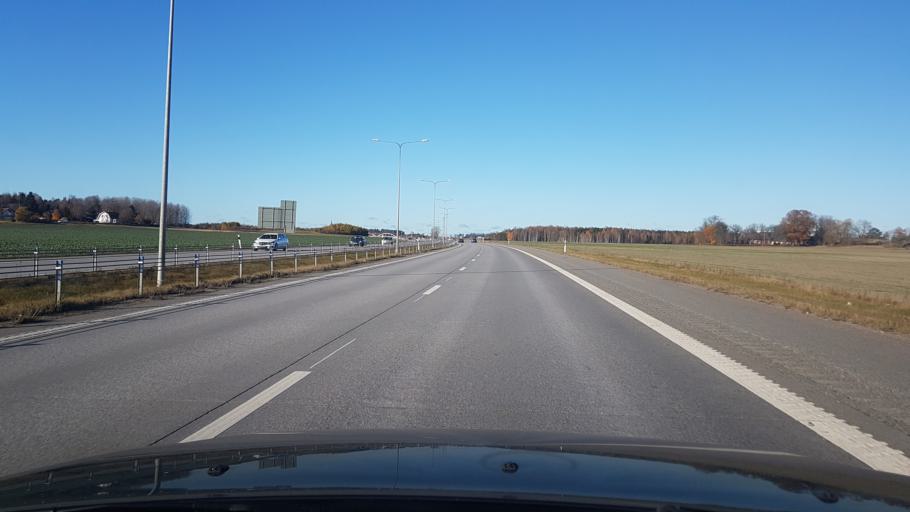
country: SE
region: Uppsala
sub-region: Uppsala Kommun
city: Saevja
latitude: 59.8599
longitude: 17.7265
